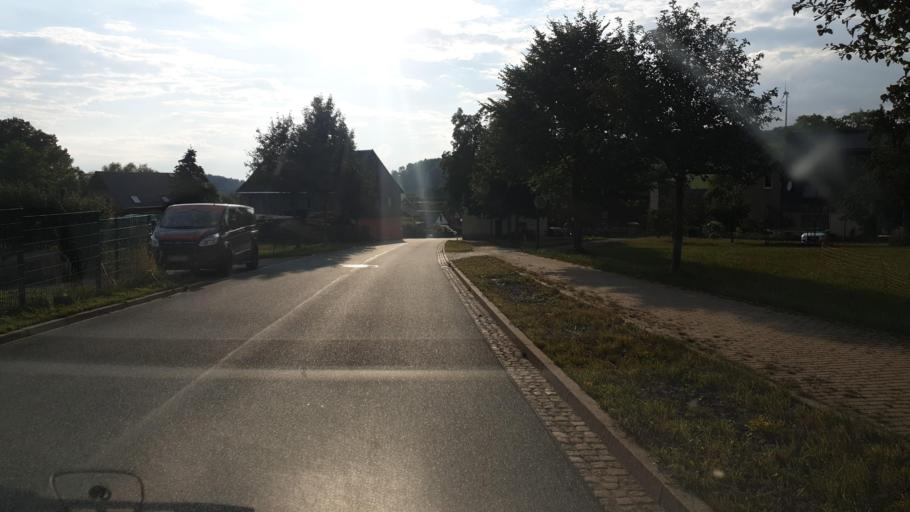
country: DE
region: Saxony
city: Zwonitz
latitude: 50.6347
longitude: 12.7824
